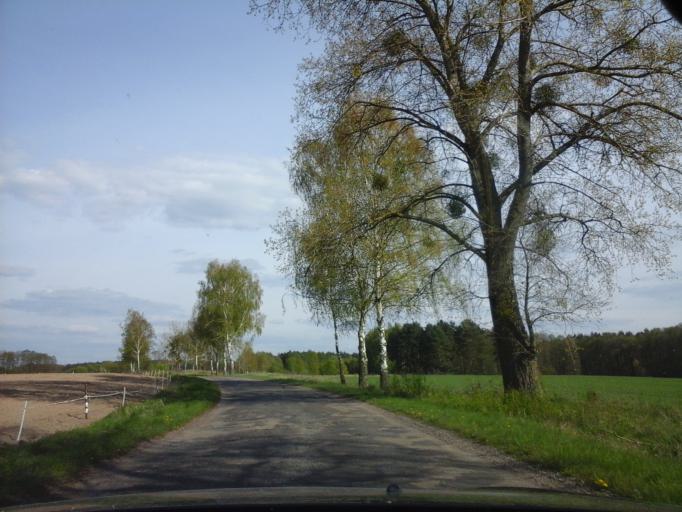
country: PL
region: West Pomeranian Voivodeship
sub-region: Powiat choszczenski
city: Bierzwnik
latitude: 53.0506
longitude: 15.6098
